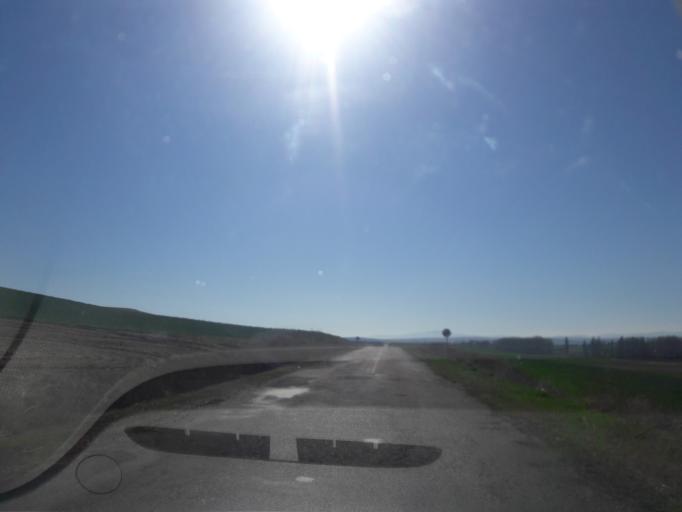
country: ES
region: Castille and Leon
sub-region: Provincia de Salamanca
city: Mancera de Abajo
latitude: 40.8295
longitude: -5.1860
